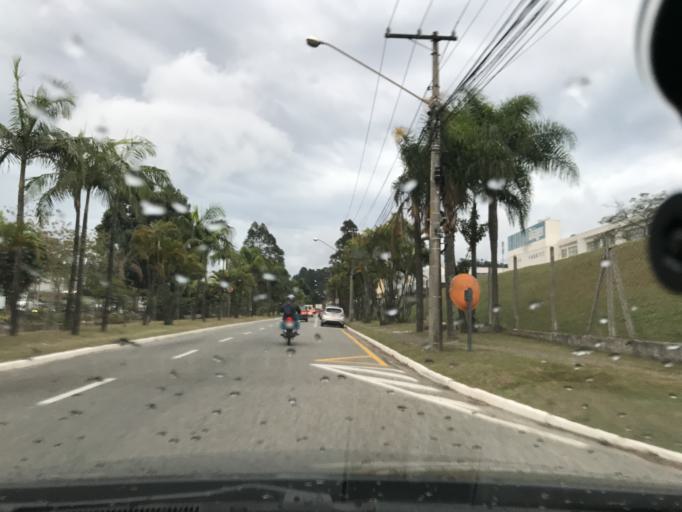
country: BR
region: Sao Paulo
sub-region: Carapicuiba
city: Carapicuiba
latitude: -23.5008
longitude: -46.8314
